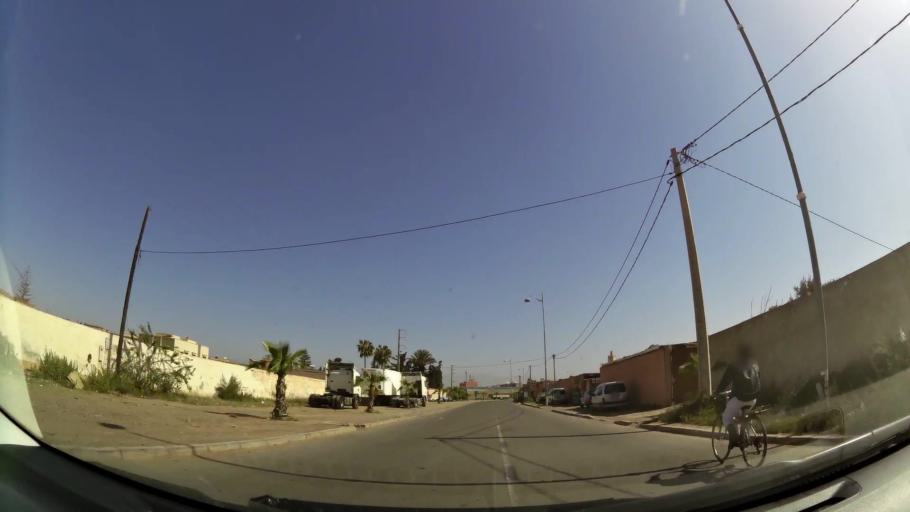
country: MA
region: Souss-Massa-Draa
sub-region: Inezgane-Ait Mellou
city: Inezgane
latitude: 30.3434
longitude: -9.5107
